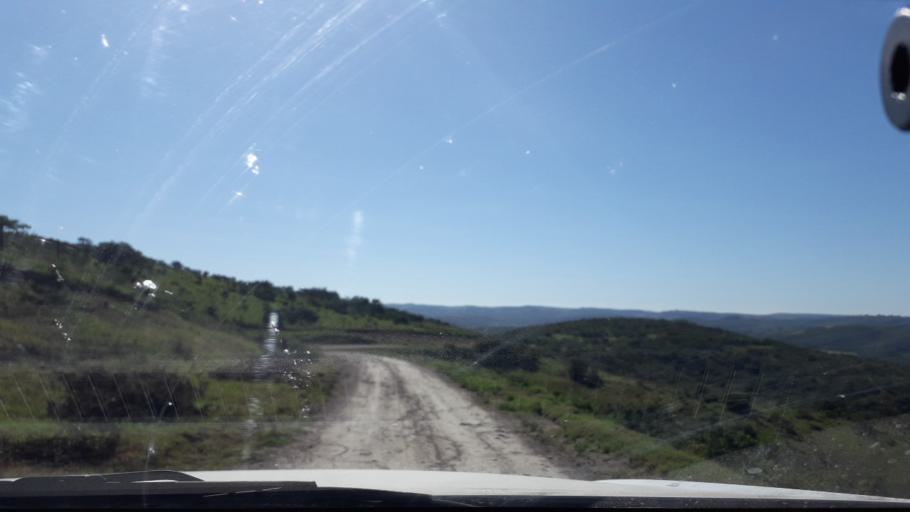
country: ZA
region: Eastern Cape
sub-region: Amathole District Municipality
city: Komga
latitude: -32.7857
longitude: 27.9559
